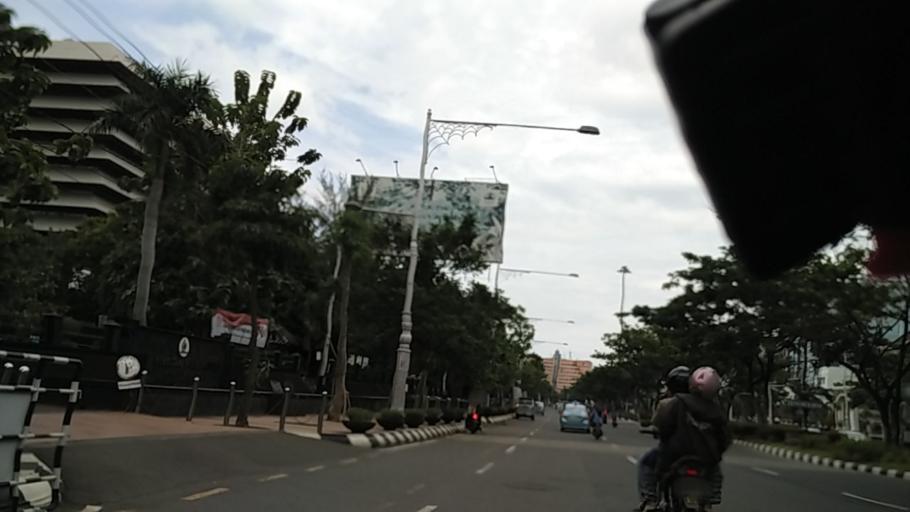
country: ID
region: Central Java
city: Semarang
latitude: -6.9956
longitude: 110.4200
